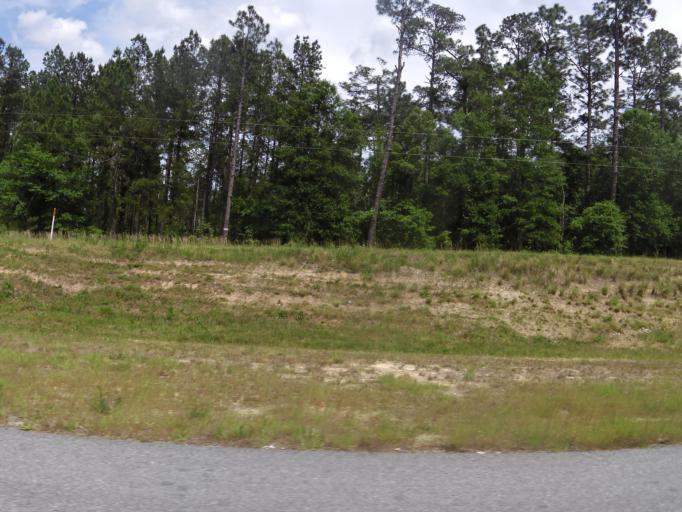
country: US
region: Georgia
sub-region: Emanuel County
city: Swainsboro
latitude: 32.7129
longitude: -82.3912
